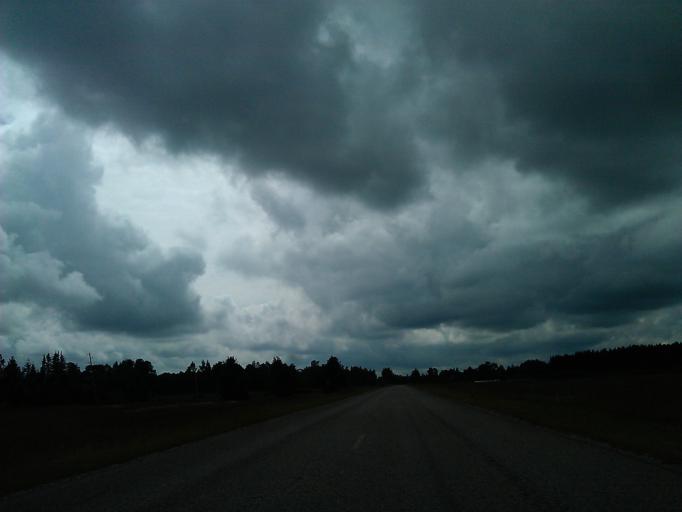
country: LV
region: Aizpute
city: Aizpute
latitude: 56.7883
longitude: 21.6520
